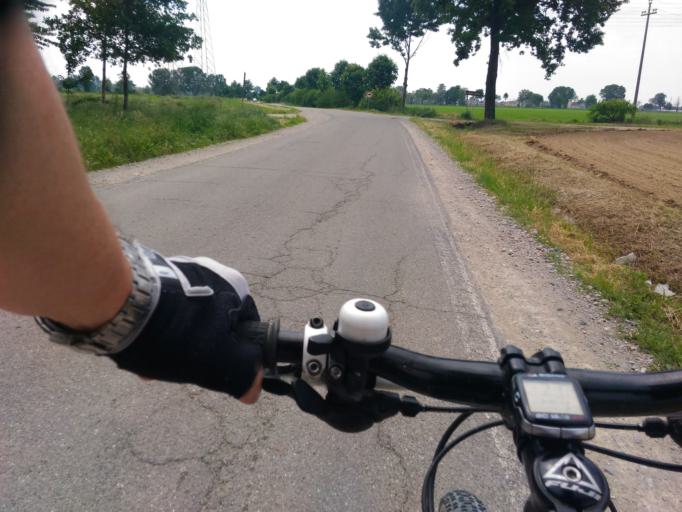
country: IT
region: Lombardy
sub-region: Provincia di Lodi
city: Quartiano
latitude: 45.3476
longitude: 9.4119
